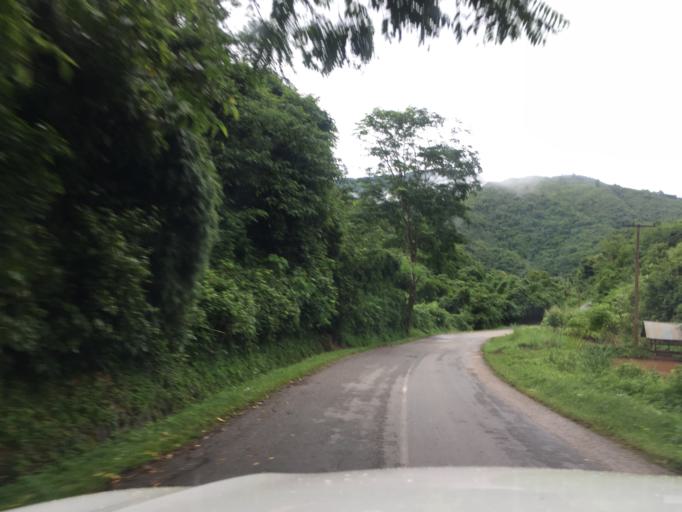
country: LA
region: Oudomxai
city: Muang La
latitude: 20.7956
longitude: 102.0856
